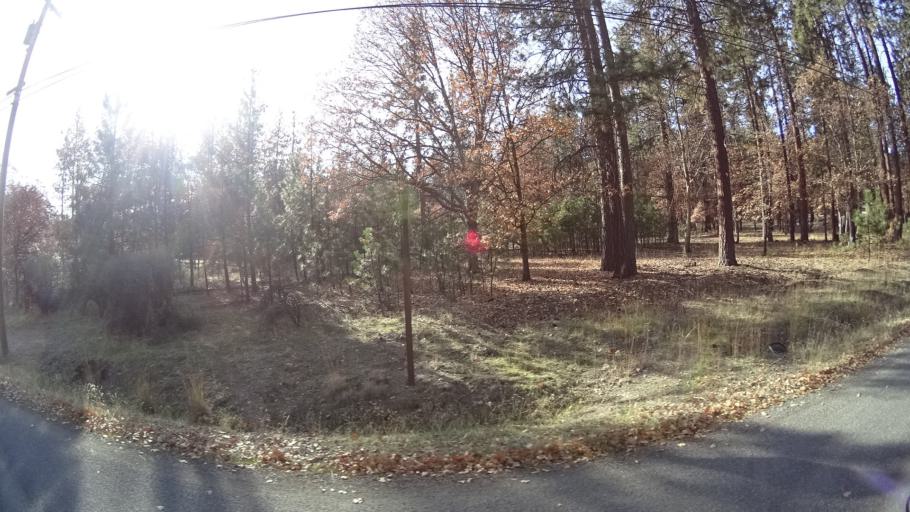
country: US
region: California
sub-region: Siskiyou County
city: Yreka
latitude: 41.6766
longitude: -122.6387
